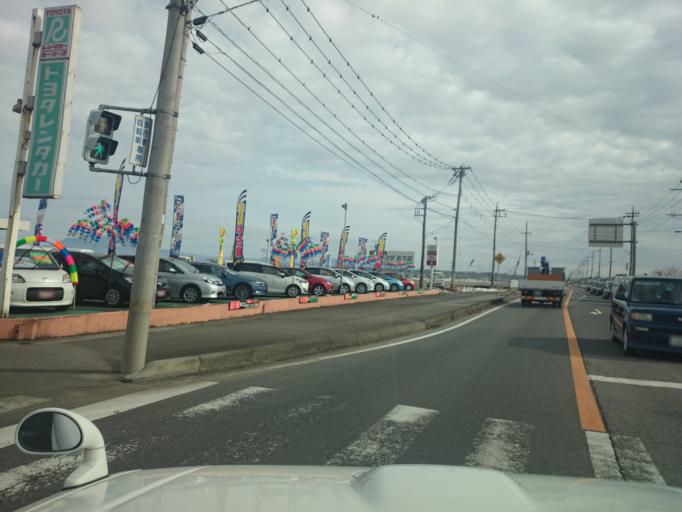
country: JP
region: Ibaraki
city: Ishige
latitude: 36.1096
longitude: 139.9841
